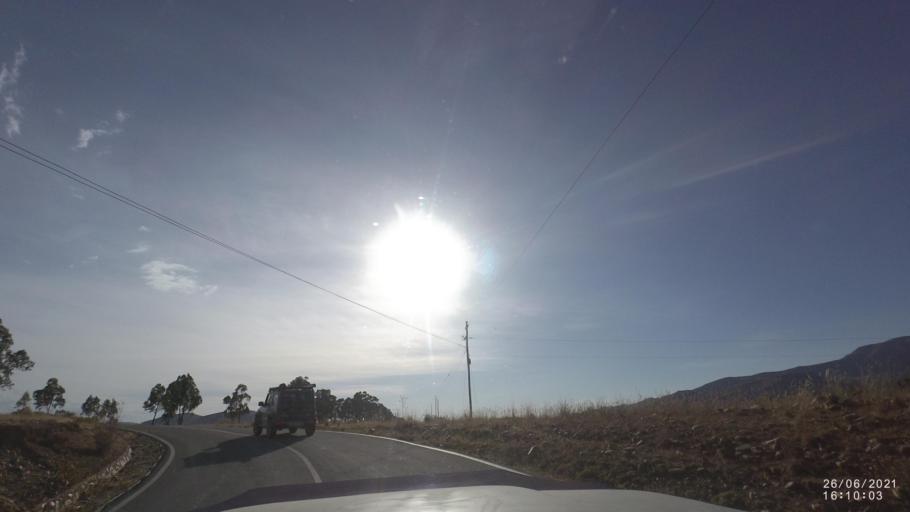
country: BO
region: Cochabamba
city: Arani
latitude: -17.8119
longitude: -65.7871
